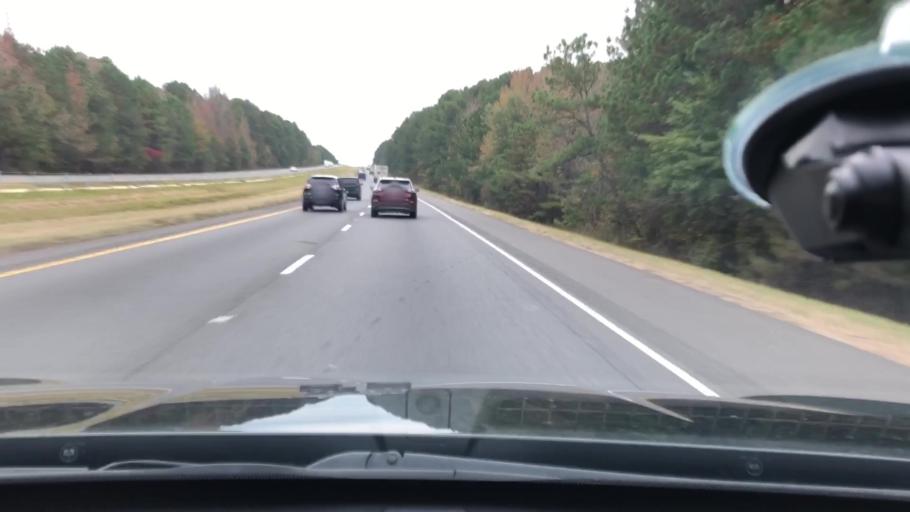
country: US
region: Arkansas
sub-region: Clark County
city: Gurdon
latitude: 34.0372
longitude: -93.1425
